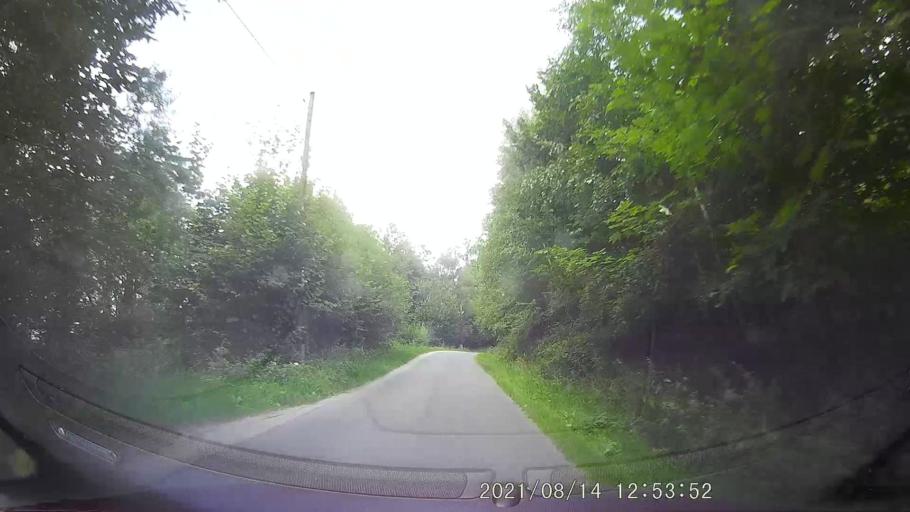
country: PL
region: Lower Silesian Voivodeship
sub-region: Powiat klodzki
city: Stronie Slaskie
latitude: 50.3234
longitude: 16.8250
